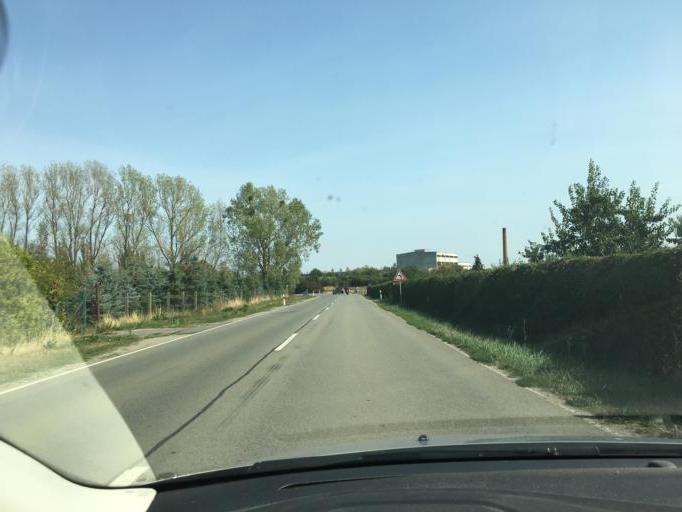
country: DE
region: Saxony-Anhalt
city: Barby
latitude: 51.9777
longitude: 11.8734
